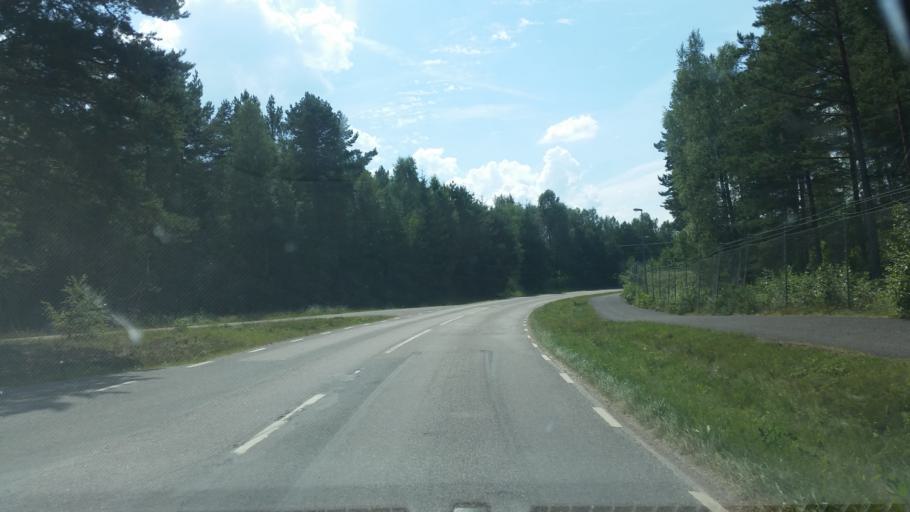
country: SE
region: Vaestra Goetaland
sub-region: Skara Kommun
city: Axvall
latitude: 58.4084
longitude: 13.5566
